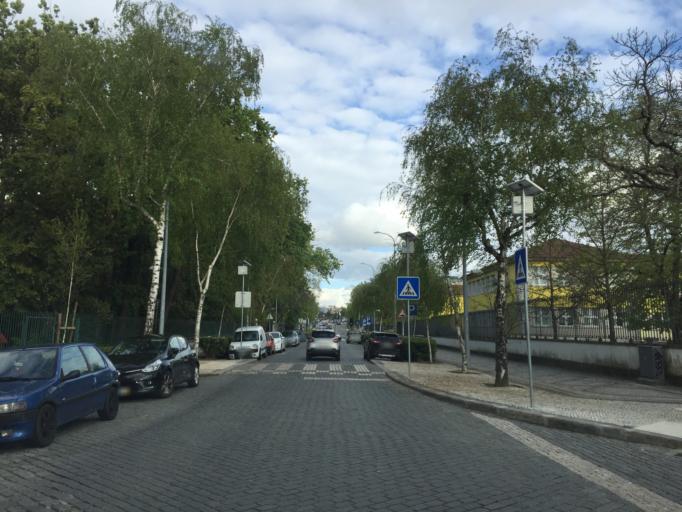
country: PT
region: Viseu
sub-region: Viseu
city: Viseu
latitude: 40.6553
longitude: -7.9175
